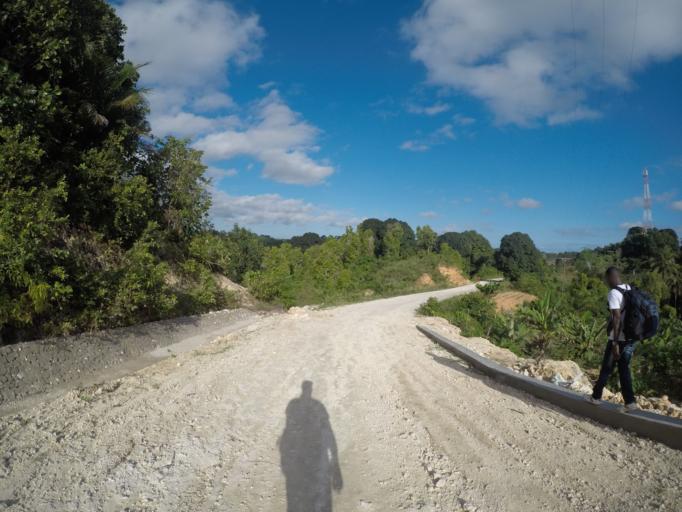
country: TZ
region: Pemba South
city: Mtambile
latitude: -5.3520
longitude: 39.7038
